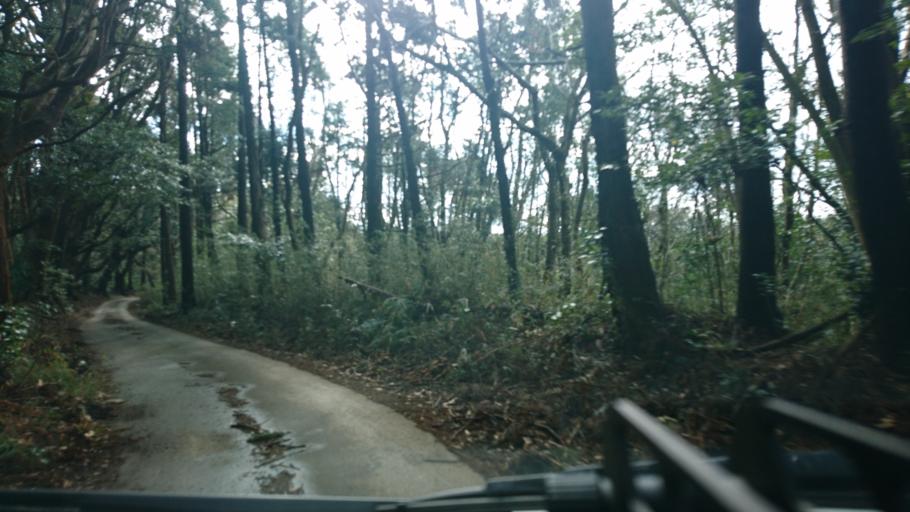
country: JP
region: Chiba
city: Kisarazu
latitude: 35.3317
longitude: 139.9613
